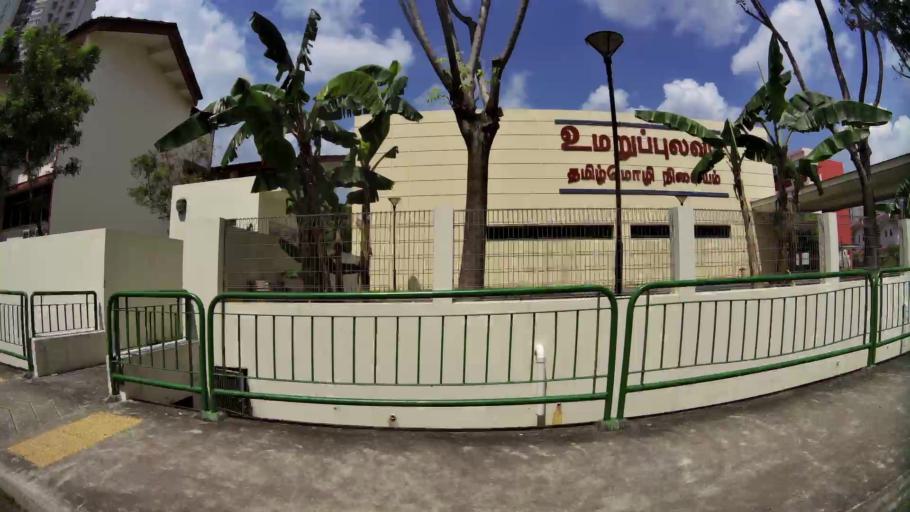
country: SG
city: Singapore
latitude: 1.3140
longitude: 103.8592
